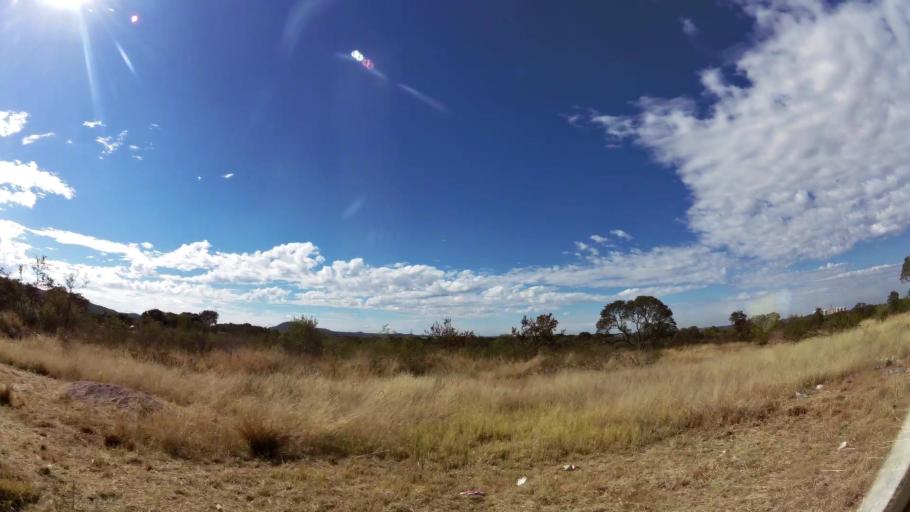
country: ZA
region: Limpopo
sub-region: Waterberg District Municipality
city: Bela-Bela
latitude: -24.8717
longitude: 28.2914
